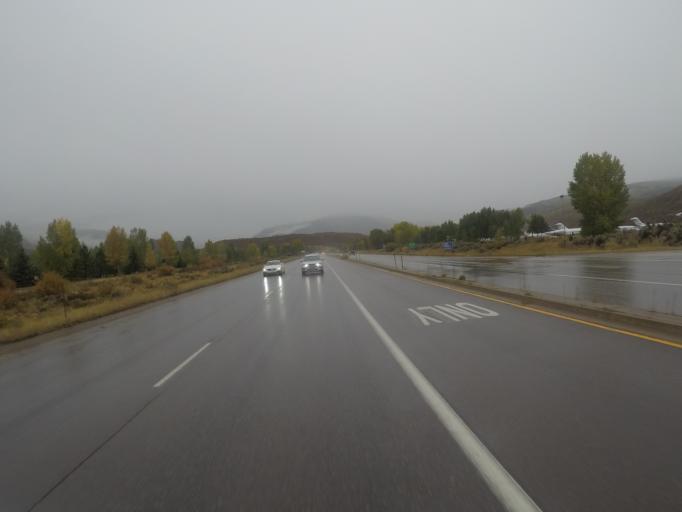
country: US
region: Colorado
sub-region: Pitkin County
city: Aspen
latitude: 39.2238
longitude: -106.8656
